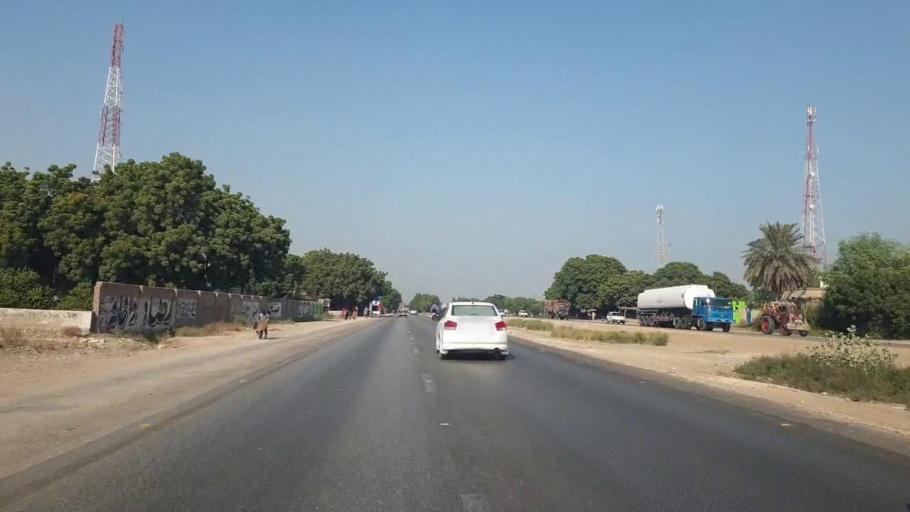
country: PK
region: Sindh
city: Matiari
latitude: 25.5017
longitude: 68.4253
